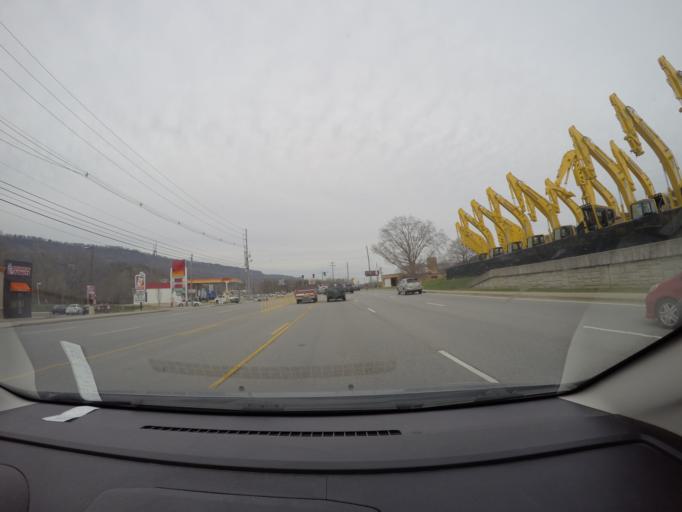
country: US
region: Tennessee
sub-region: Hamilton County
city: Signal Mountain
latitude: 35.0963
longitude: -85.3279
